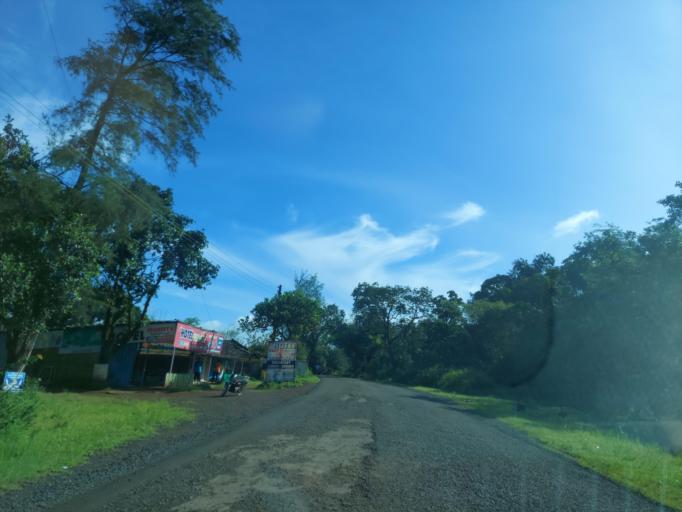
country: IN
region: Maharashtra
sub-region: Kolhapur
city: Ajra
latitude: 16.0216
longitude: 74.0540
